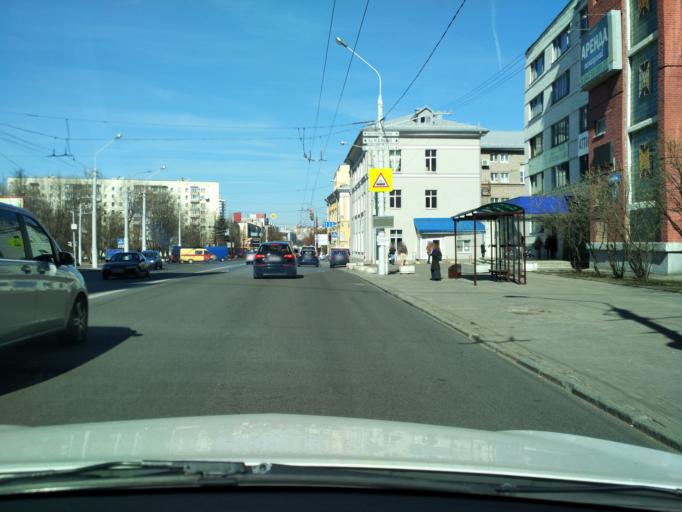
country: BY
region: Minsk
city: Minsk
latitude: 53.9152
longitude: 27.5710
